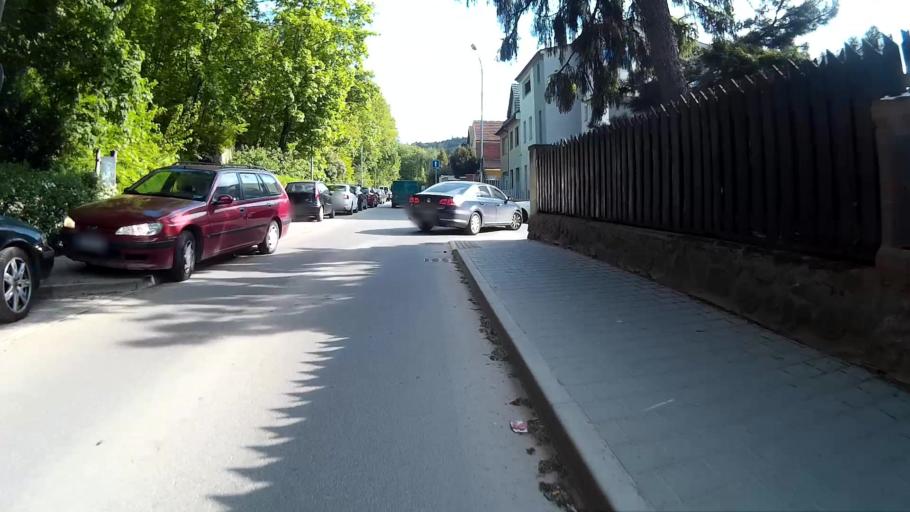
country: CZ
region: South Moravian
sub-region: Mesto Brno
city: Brno
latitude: 49.2102
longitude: 16.5782
